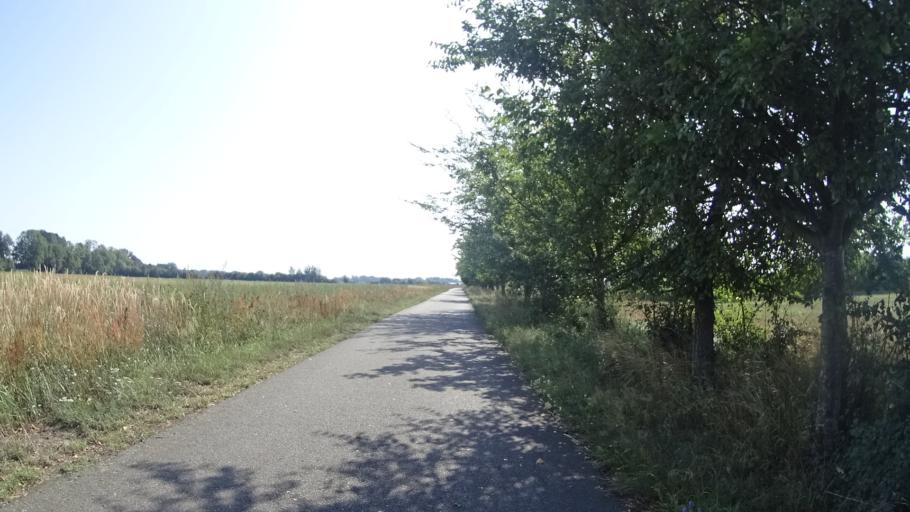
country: DE
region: Brandenburg
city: Burg
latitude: 51.8222
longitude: 14.1626
